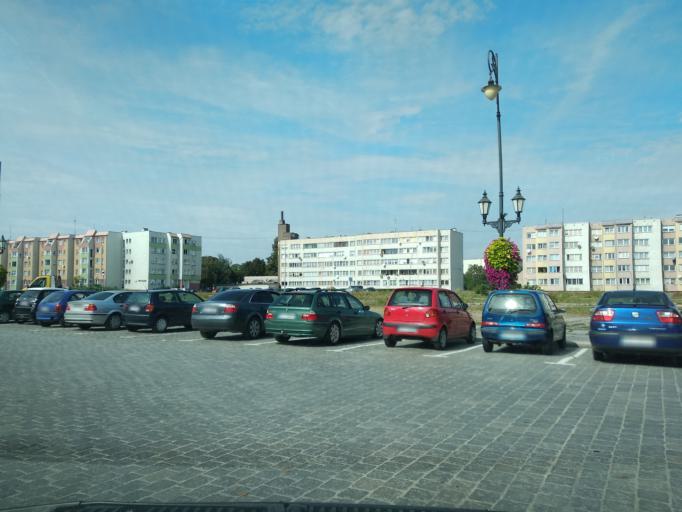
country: PL
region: Lower Silesian Voivodeship
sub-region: Powiat strzelinski
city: Strzelin
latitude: 50.7813
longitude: 17.0719
